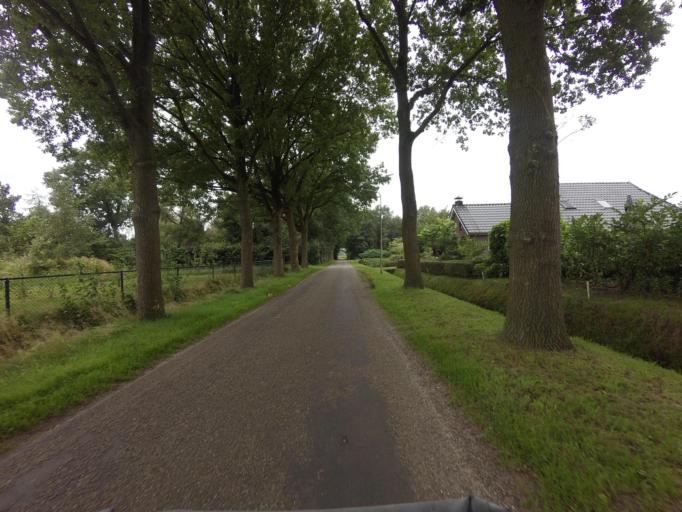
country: NL
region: Overijssel
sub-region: Gemeente Steenwijkerland
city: Steenwijkerwold
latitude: 52.8271
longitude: 6.0852
